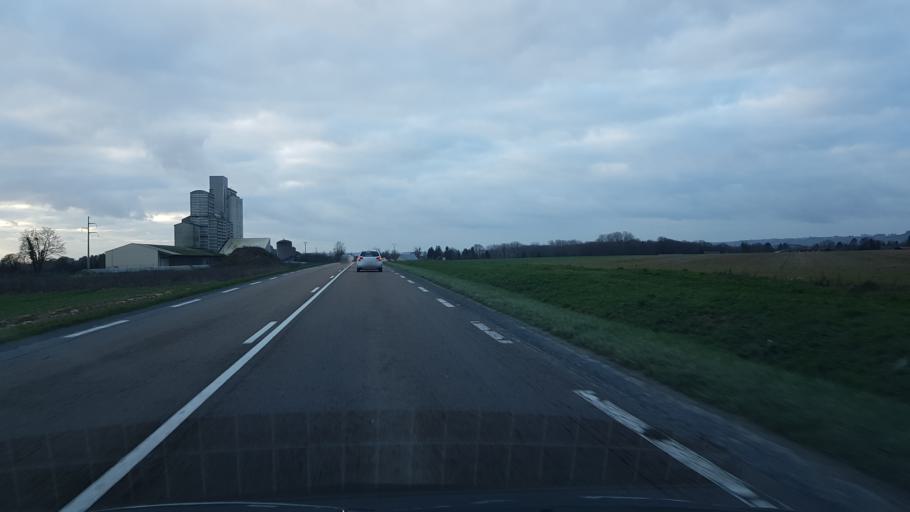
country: FR
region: Champagne-Ardenne
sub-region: Departement de la Marne
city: Connantre
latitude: 48.7265
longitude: 3.8584
